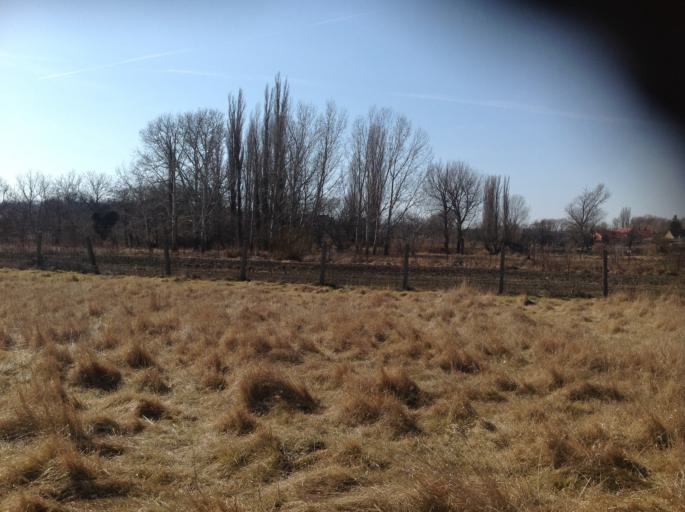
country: HU
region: Pest
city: Soskut
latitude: 47.4053
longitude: 18.8320
